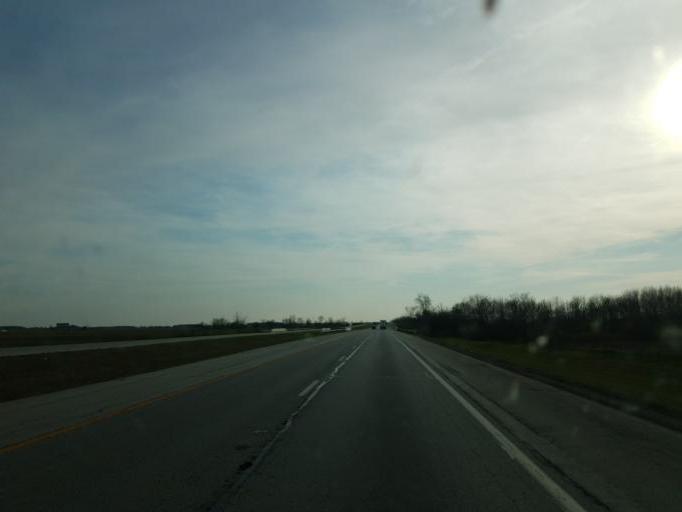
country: US
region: Ohio
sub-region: Greene County
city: Jamestown
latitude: 39.5759
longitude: -83.6895
